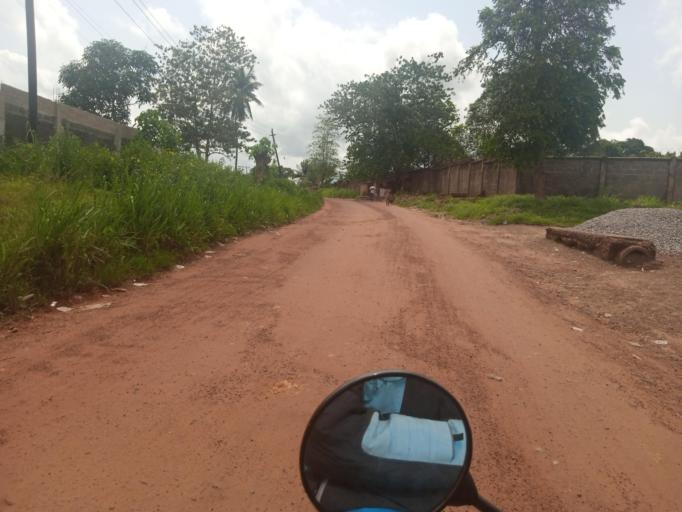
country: SL
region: Southern Province
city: Bo
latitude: 7.9647
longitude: -11.7449
